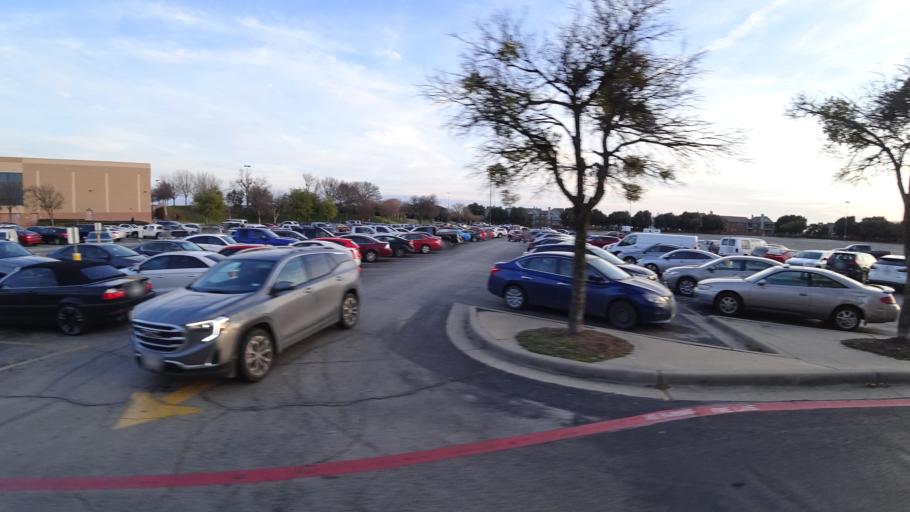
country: US
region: Texas
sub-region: Denton County
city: Lewisville
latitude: 33.0016
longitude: -96.9721
